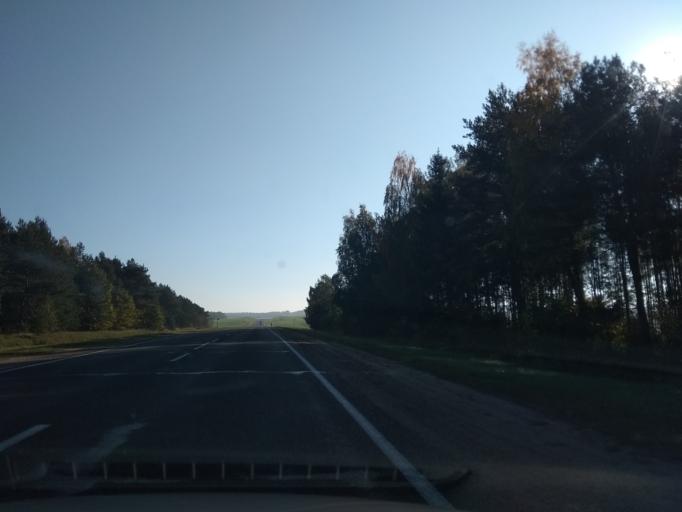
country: BY
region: Grodnenskaya
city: Zel'va
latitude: 53.1460
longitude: 24.8605
